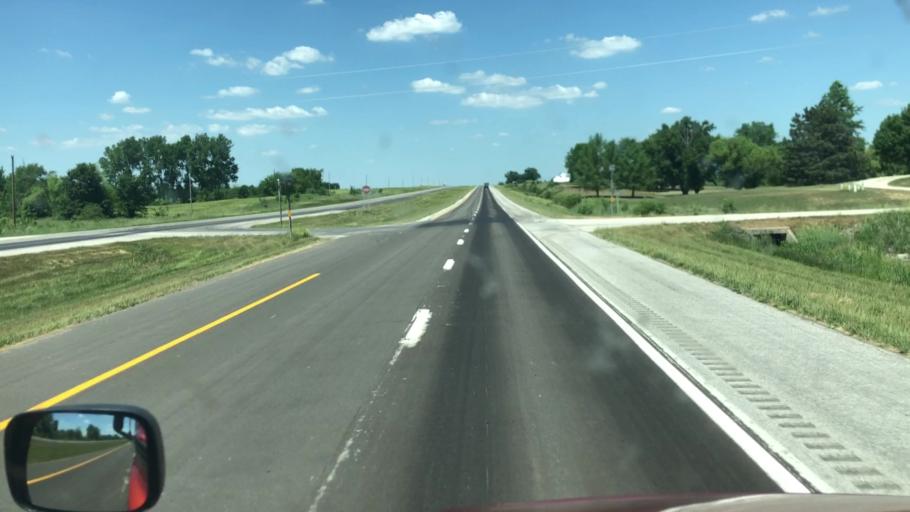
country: US
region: Missouri
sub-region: Macon County
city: La Plata
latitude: 39.9984
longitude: -92.4752
